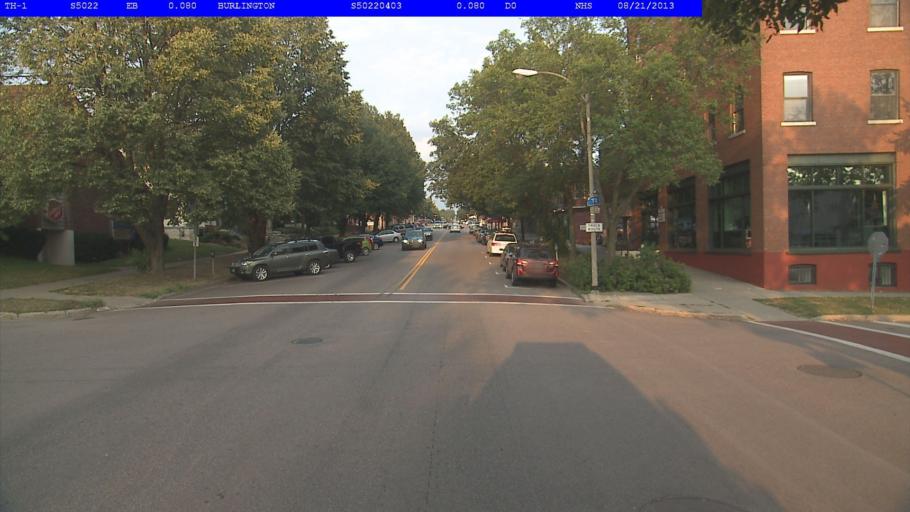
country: US
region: Vermont
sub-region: Chittenden County
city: Burlington
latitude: 44.4757
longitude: -73.2172
